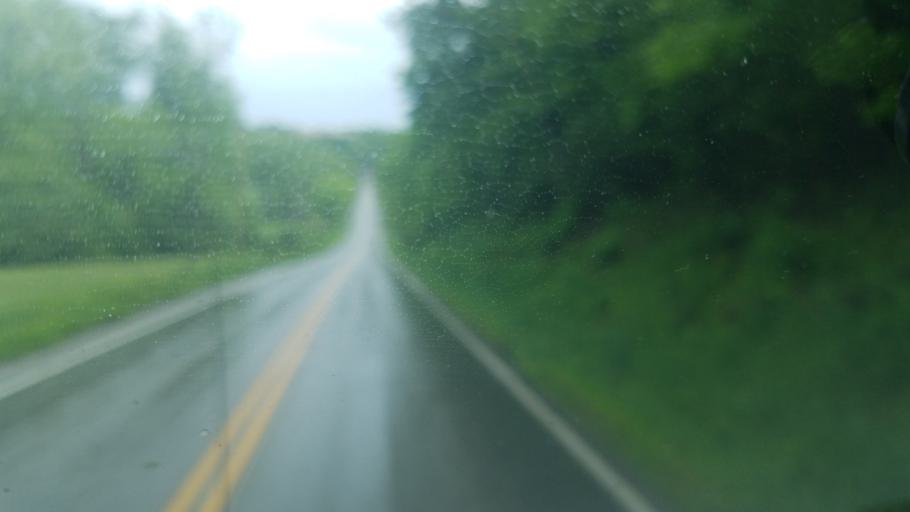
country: US
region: Ohio
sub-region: Wayne County
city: Wooster
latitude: 40.8014
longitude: -81.9055
